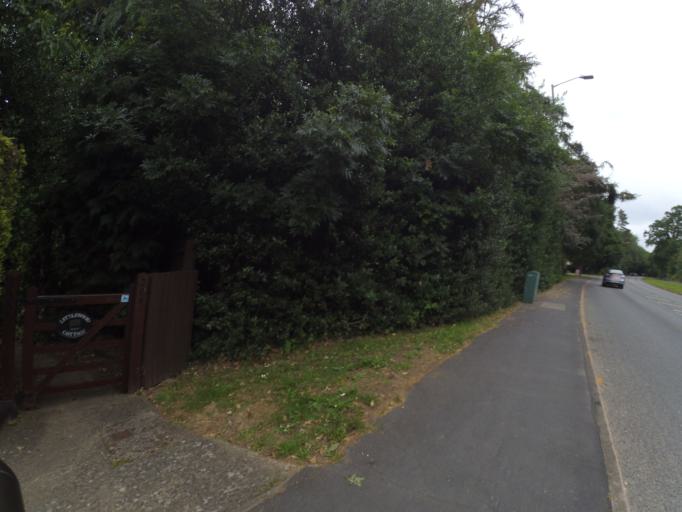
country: GB
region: England
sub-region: Warwickshire
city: Dunchurch
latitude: 52.3506
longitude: -1.2762
